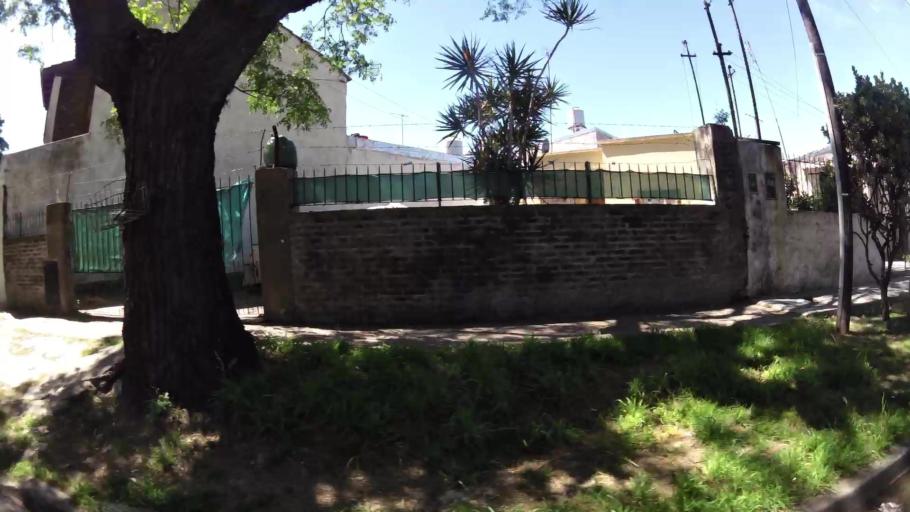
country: AR
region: Buenos Aires
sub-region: Partido de San Isidro
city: San Isidro
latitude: -34.5067
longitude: -58.5768
